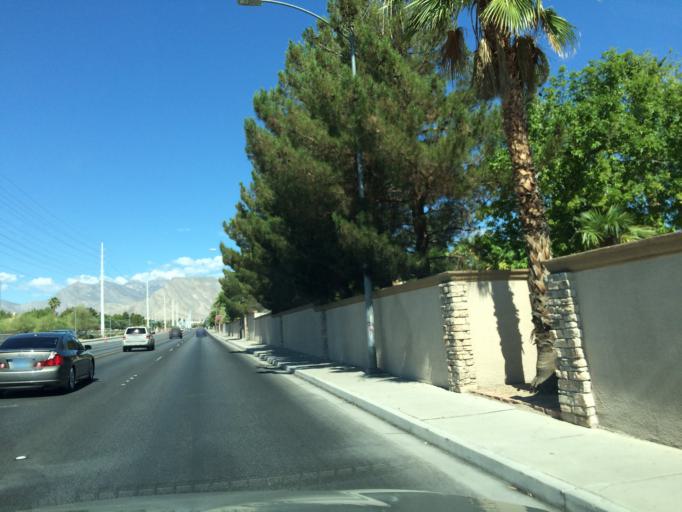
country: US
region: Nevada
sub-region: Clark County
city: Spring Valley
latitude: 36.2186
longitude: -115.2701
